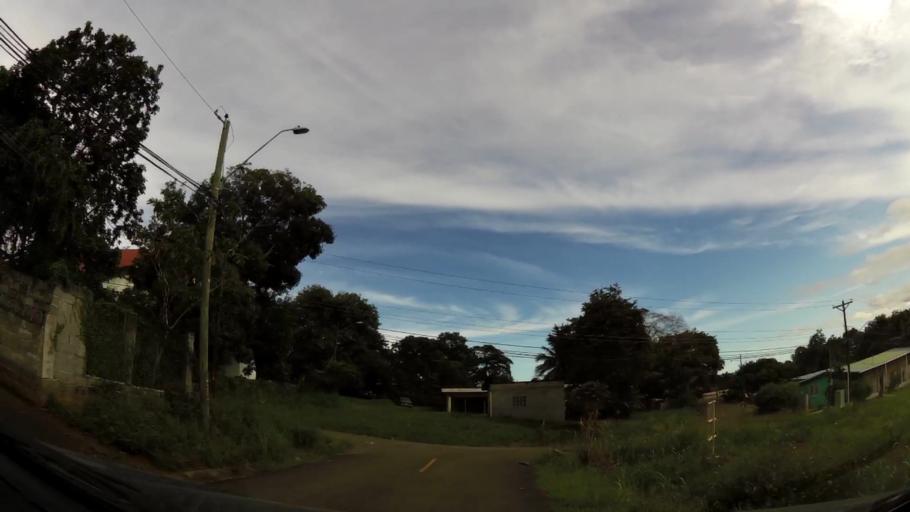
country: PA
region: Panama
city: El Coco
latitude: 8.8677
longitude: -79.8095
